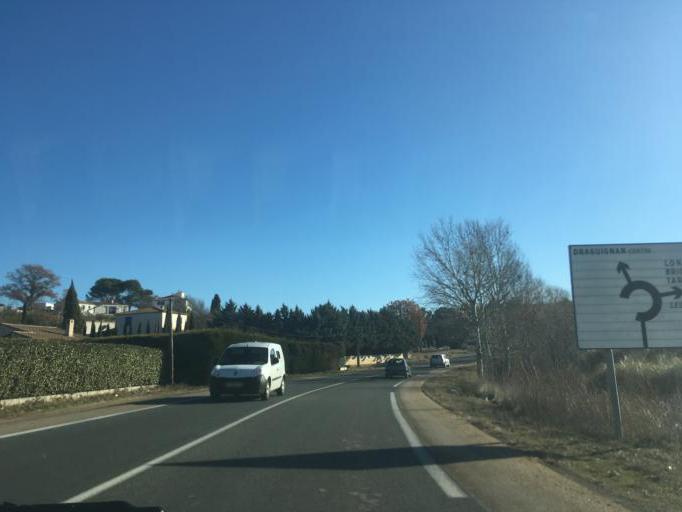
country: FR
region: Provence-Alpes-Cote d'Azur
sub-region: Departement du Var
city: Draguignan
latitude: 43.5276
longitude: 6.4348
